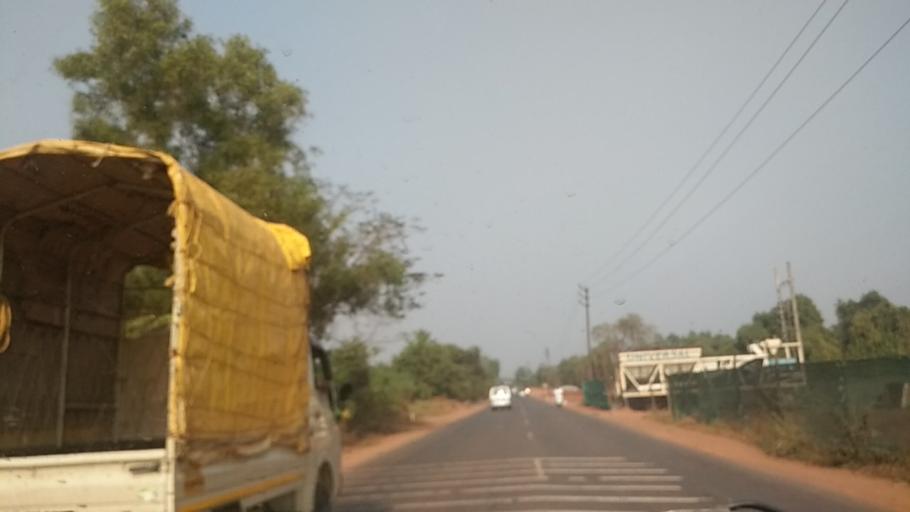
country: IN
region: Goa
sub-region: North Goa
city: Mapuca
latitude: 15.5894
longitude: 73.8219
